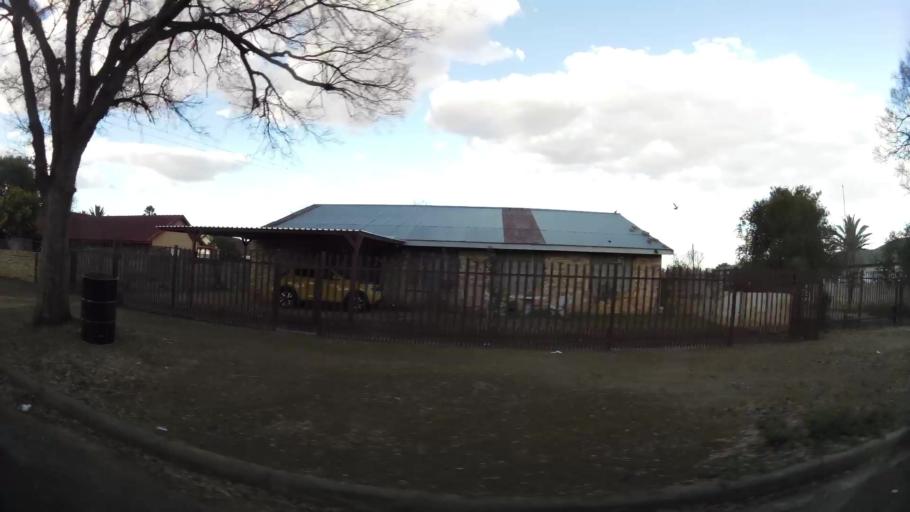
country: ZA
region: North-West
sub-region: Dr Kenneth Kaunda District Municipality
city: Potchefstroom
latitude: -26.7358
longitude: 27.0909
